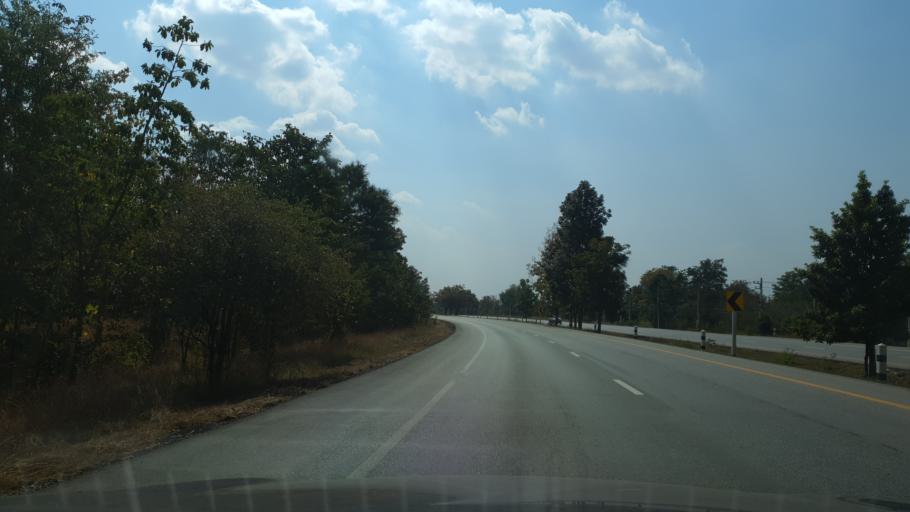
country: TH
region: Tak
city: Sam Ngao
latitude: 17.2962
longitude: 99.1434
